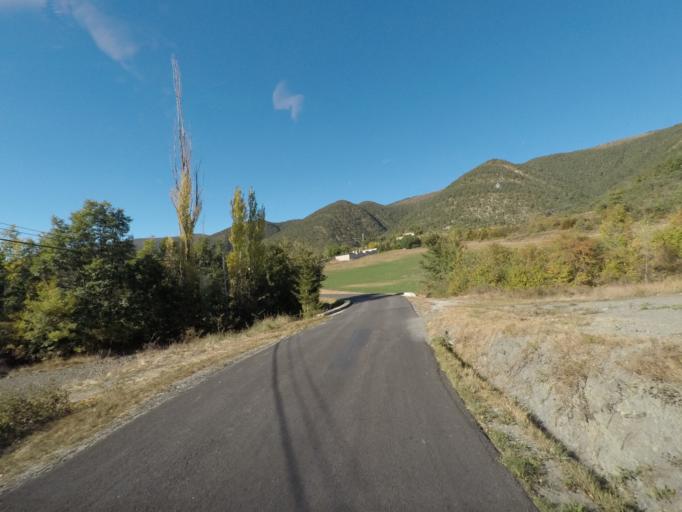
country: FR
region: Provence-Alpes-Cote d'Azur
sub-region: Departement des Hautes-Alpes
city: Serres
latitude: 44.4632
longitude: 5.5223
